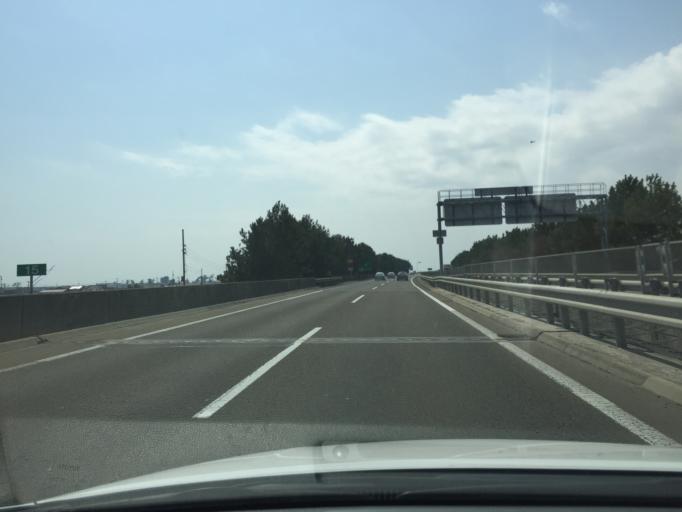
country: JP
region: Miyagi
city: Sendai
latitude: 38.1956
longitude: 140.9412
